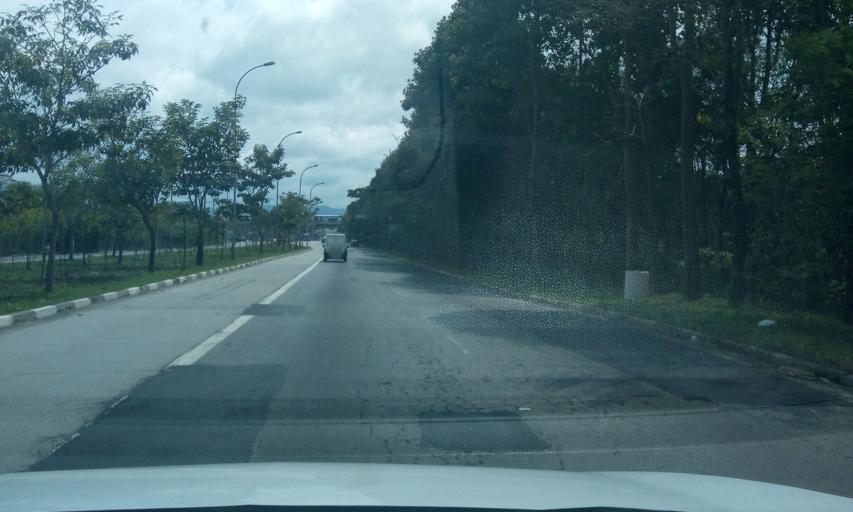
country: BR
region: Sao Paulo
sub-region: Guarulhos
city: Guarulhos
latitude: -23.4510
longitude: -46.4933
